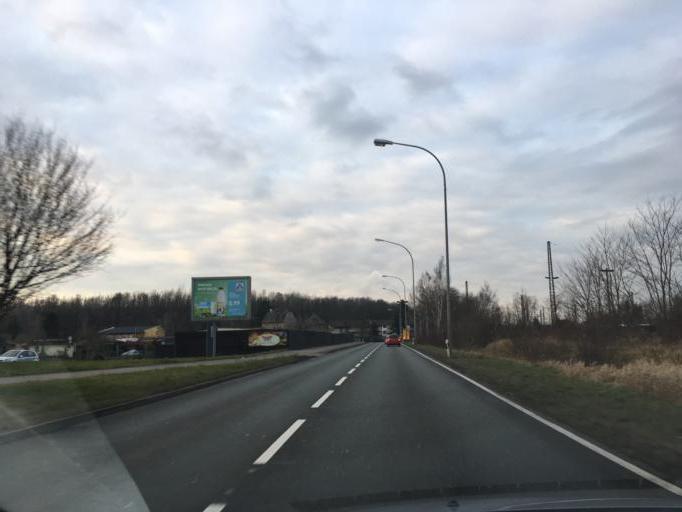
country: DE
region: Saxony
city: Borna
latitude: 51.1170
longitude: 12.4856
